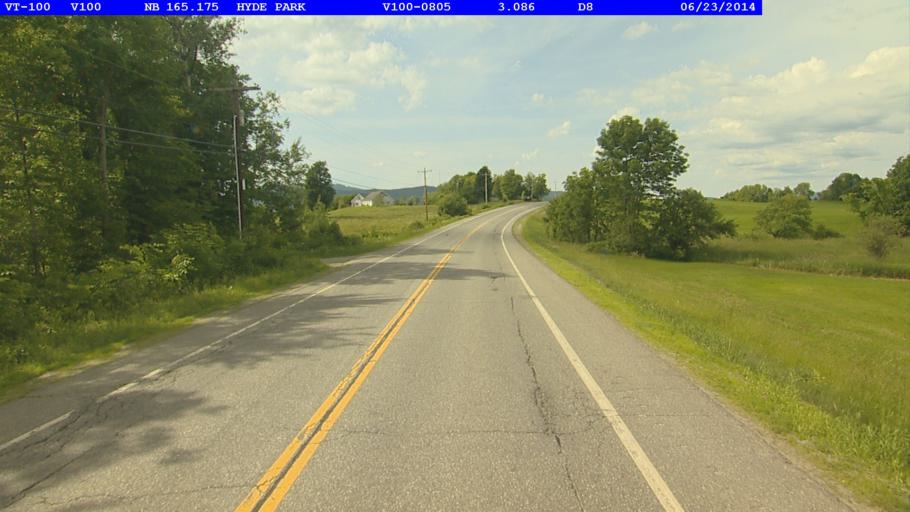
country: US
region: Vermont
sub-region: Lamoille County
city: Hyde Park
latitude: 44.6390
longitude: -72.5971
